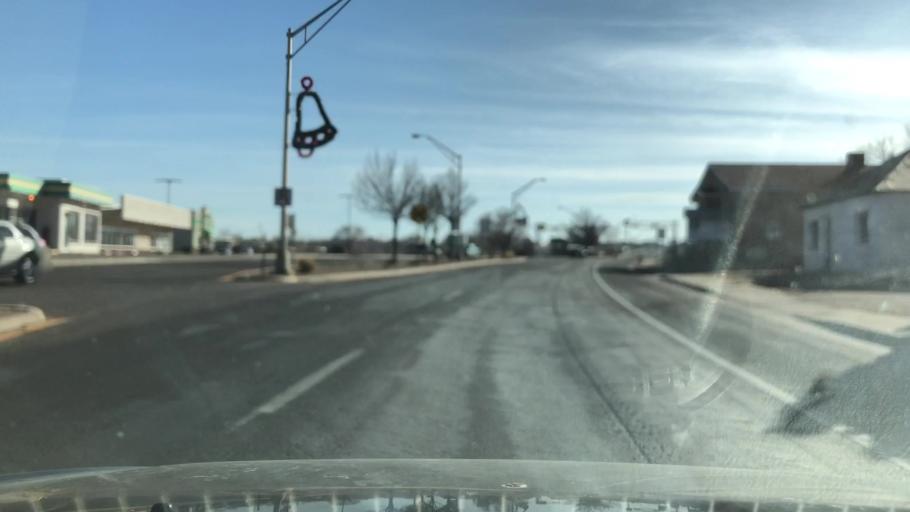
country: US
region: New Mexico
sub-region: Socorro County
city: Socorro
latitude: 34.0527
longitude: -106.8914
